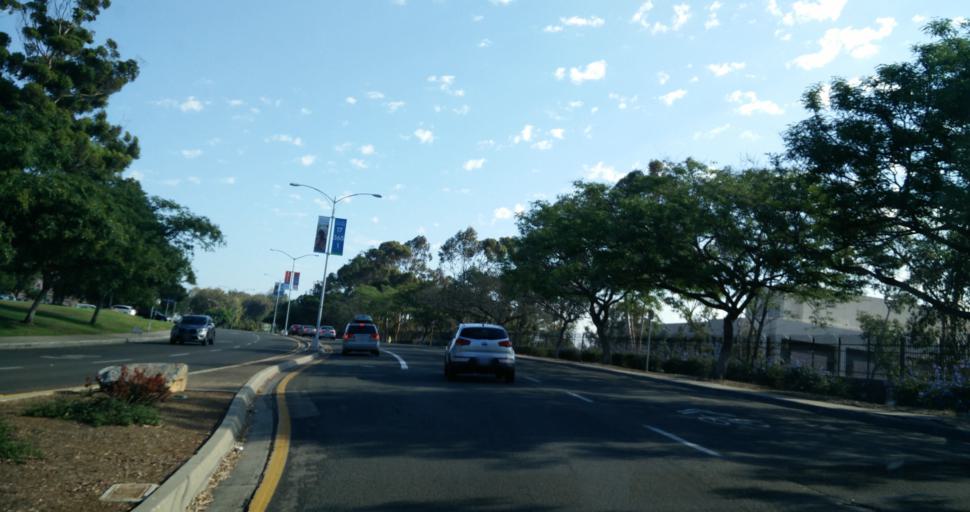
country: US
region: California
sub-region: San Diego County
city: San Diego
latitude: 32.7285
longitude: -117.1466
